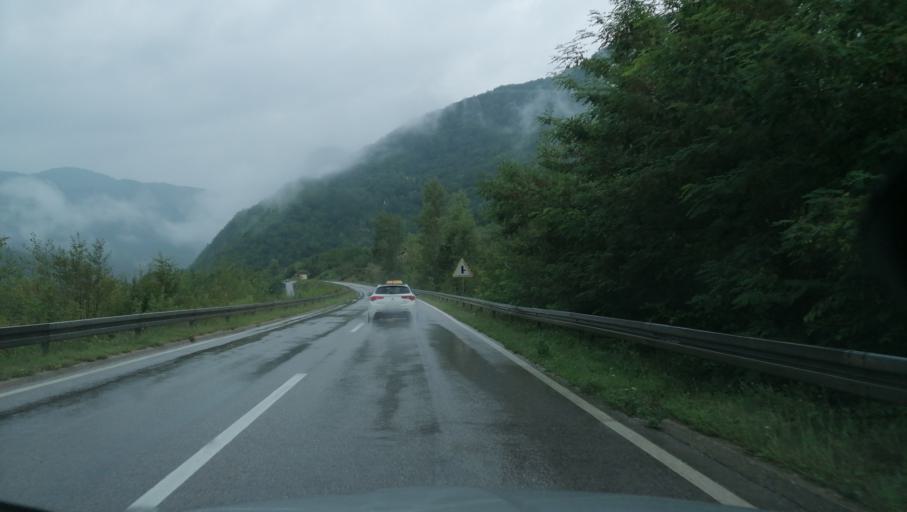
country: BA
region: Republika Srpska
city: Visegrad
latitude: 43.7179
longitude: 19.1685
